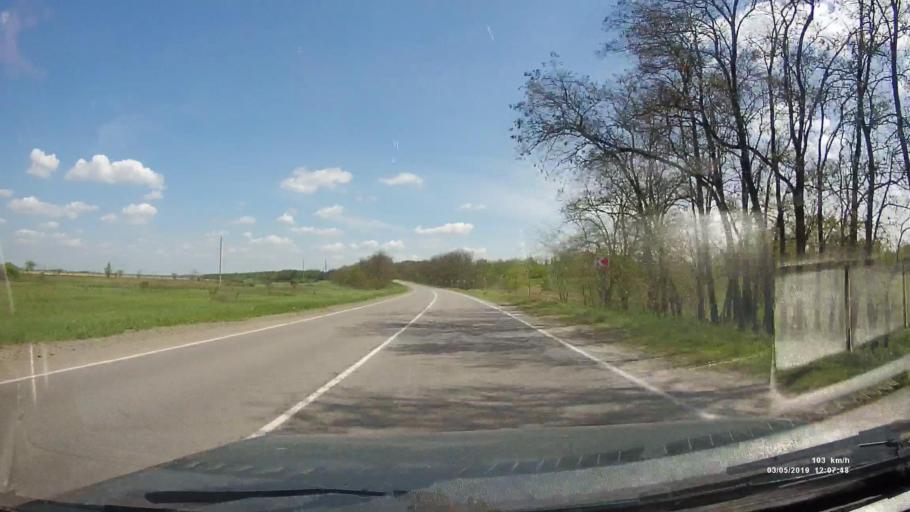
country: RU
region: Rostov
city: Bagayevskaya
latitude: 47.2843
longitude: 40.4835
